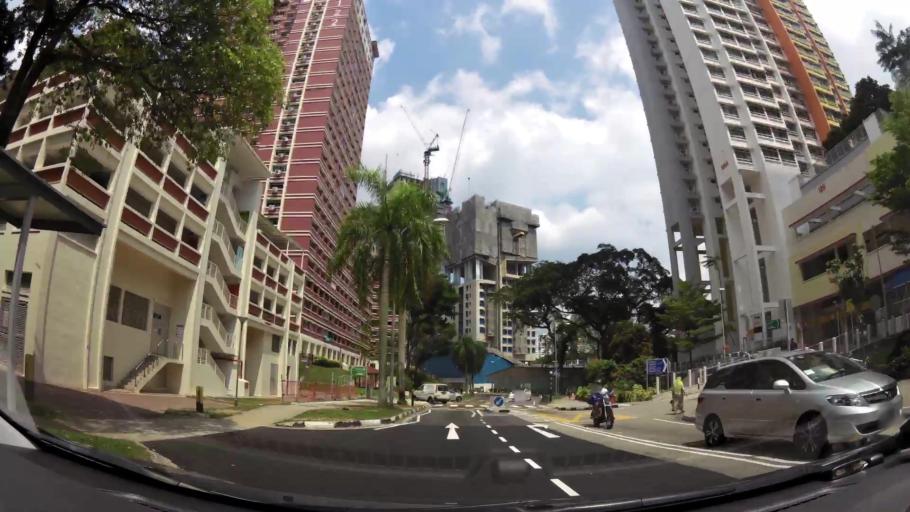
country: SG
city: Singapore
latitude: 1.2827
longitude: 103.8289
